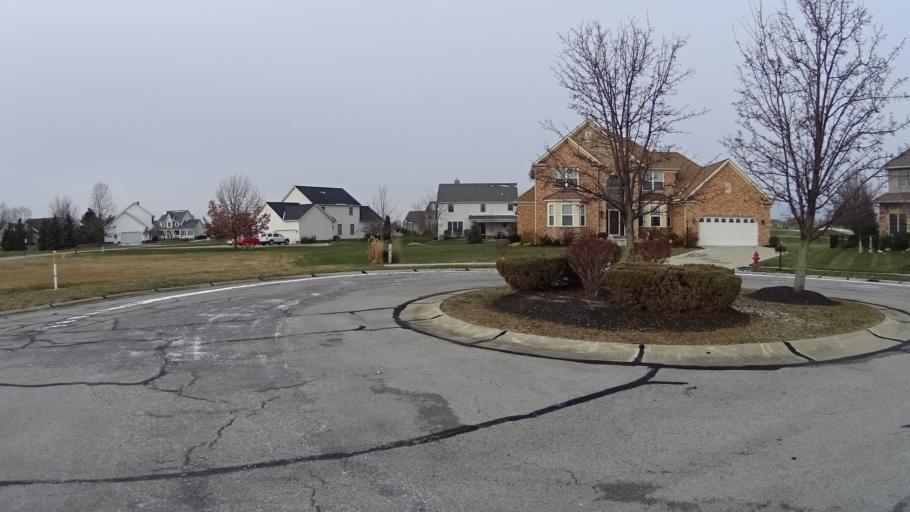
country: US
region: Ohio
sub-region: Lorain County
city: Lagrange
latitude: 41.2478
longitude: -82.1133
